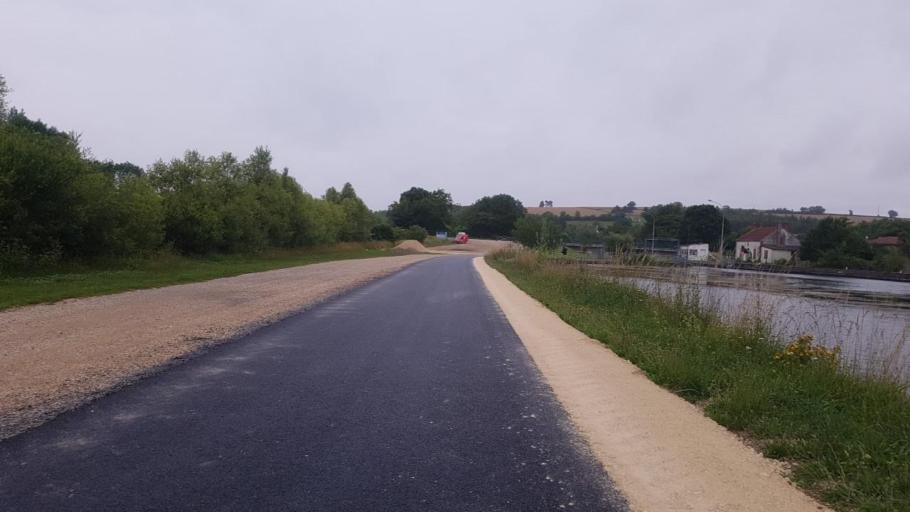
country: FR
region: Champagne-Ardenne
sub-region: Departement de la Marne
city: Vitry-le-Francois
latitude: 48.7895
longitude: 4.5336
